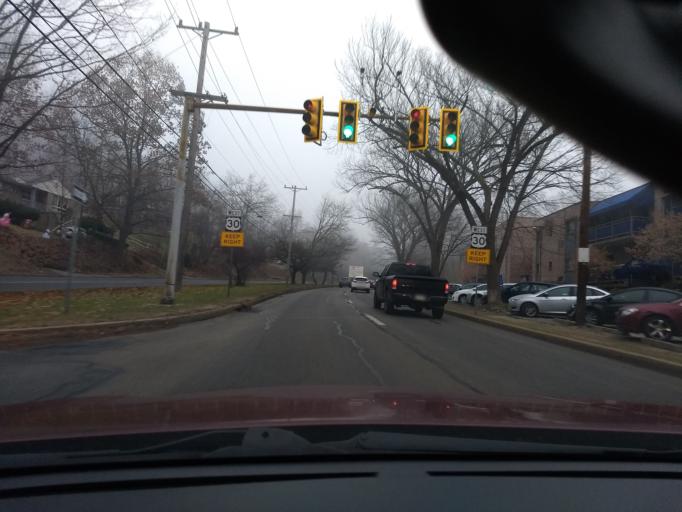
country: US
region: Pennsylvania
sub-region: Allegheny County
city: Braddock Hills
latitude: 40.4272
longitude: -79.8629
